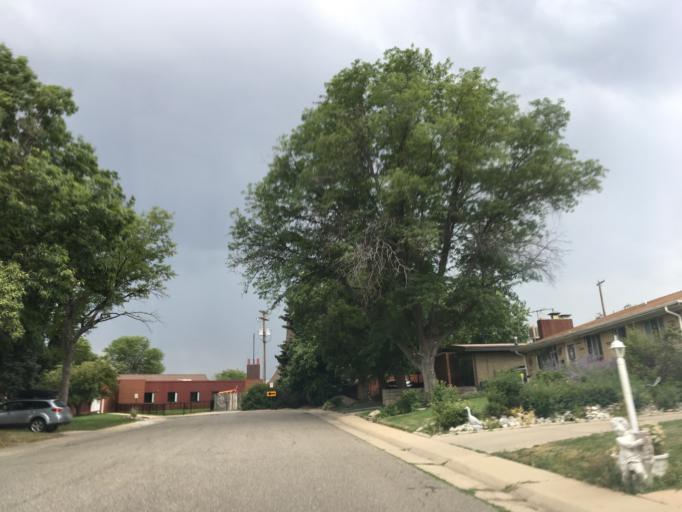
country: US
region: Colorado
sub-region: Arapahoe County
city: Sheridan
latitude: 39.6692
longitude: -105.0429
